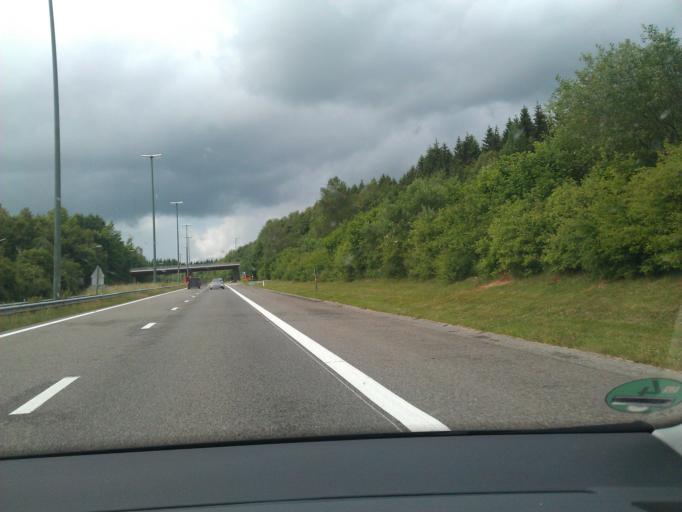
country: BE
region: Wallonia
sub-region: Province de Liege
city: Saint-Vith
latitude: 50.2525
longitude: 6.1703
